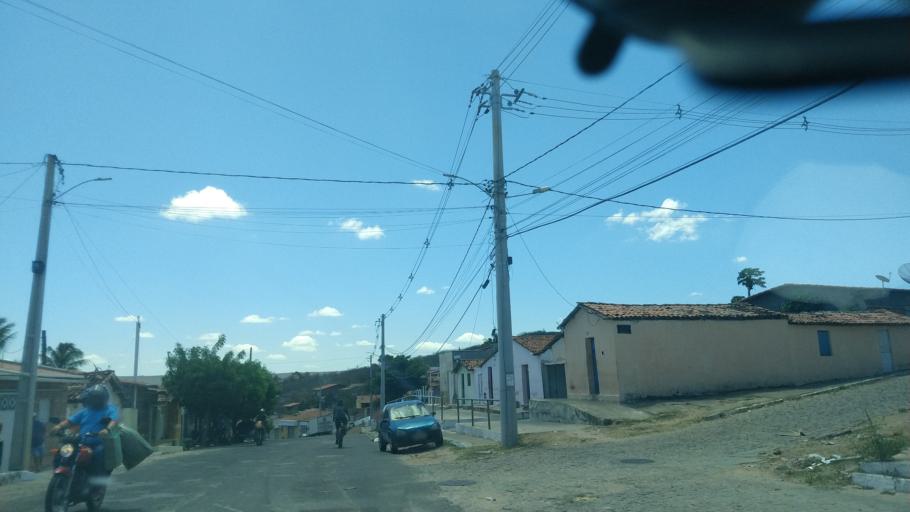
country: BR
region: Rio Grande do Norte
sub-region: Cerro Cora
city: Cerro Cora
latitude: -6.0355
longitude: -36.3467
